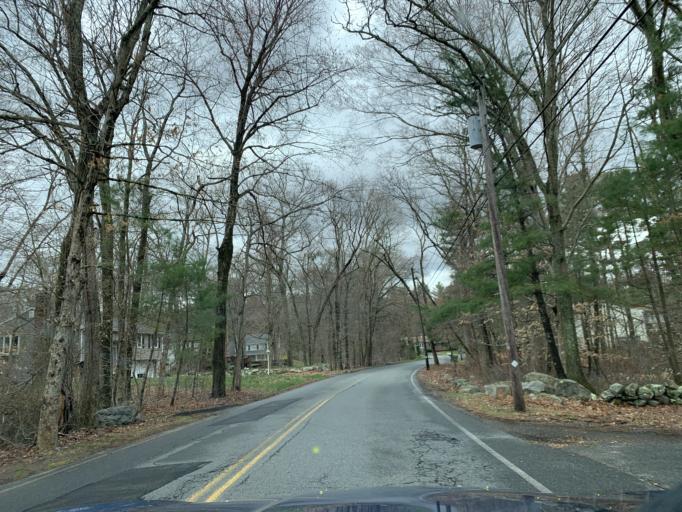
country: US
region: Massachusetts
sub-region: Bristol County
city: Norton
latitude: 41.9355
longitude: -71.2211
